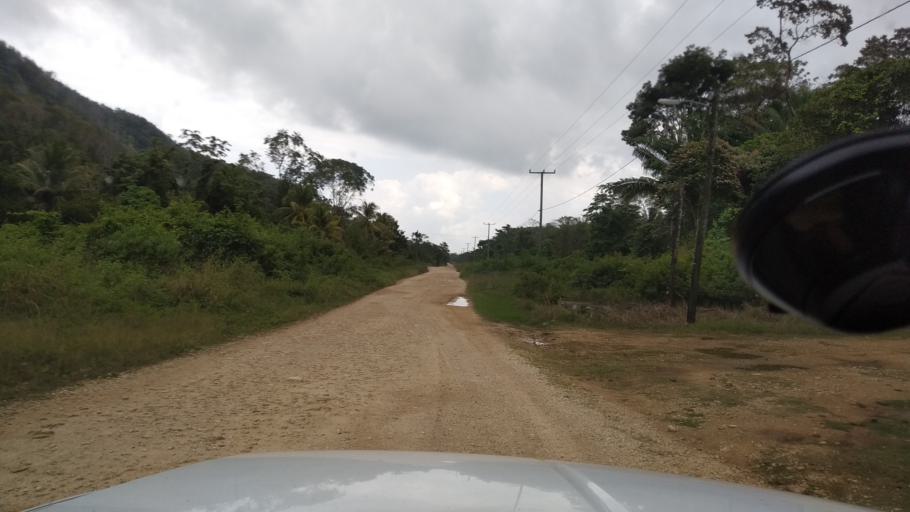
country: BZ
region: Toledo
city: Punta Gorda
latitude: 16.2125
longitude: -89.0180
